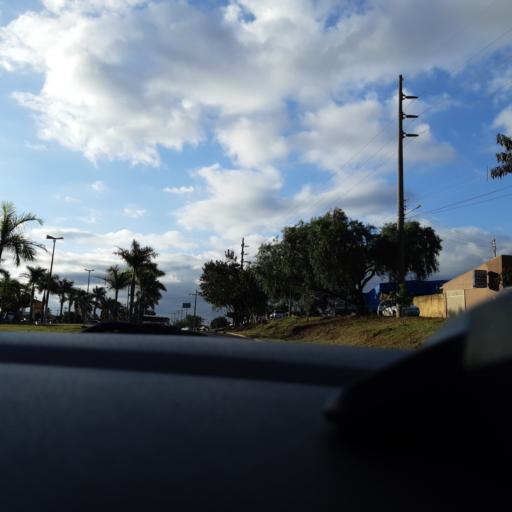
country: BR
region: Sao Paulo
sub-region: Ourinhos
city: Ourinhos
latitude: -22.9862
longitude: -49.8556
